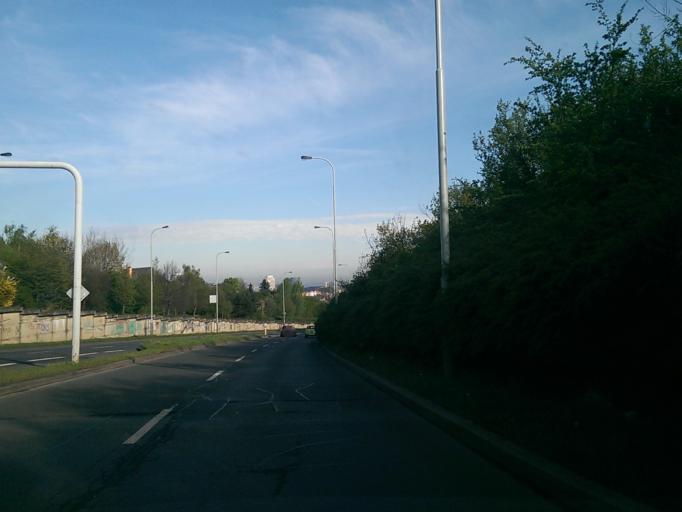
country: CZ
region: Central Bohemia
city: Vestec
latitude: 50.0346
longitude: 14.4814
